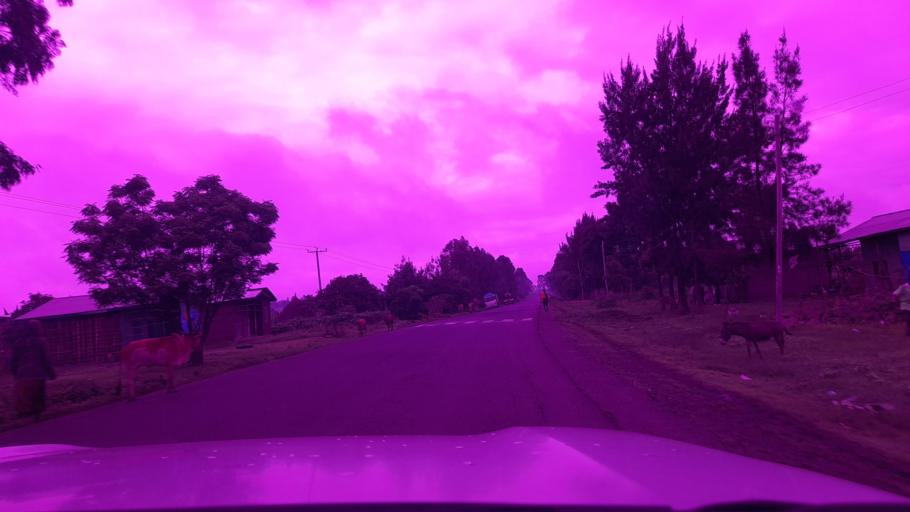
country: ET
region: Oromiya
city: Waliso
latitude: 8.2747
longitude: 37.6667
